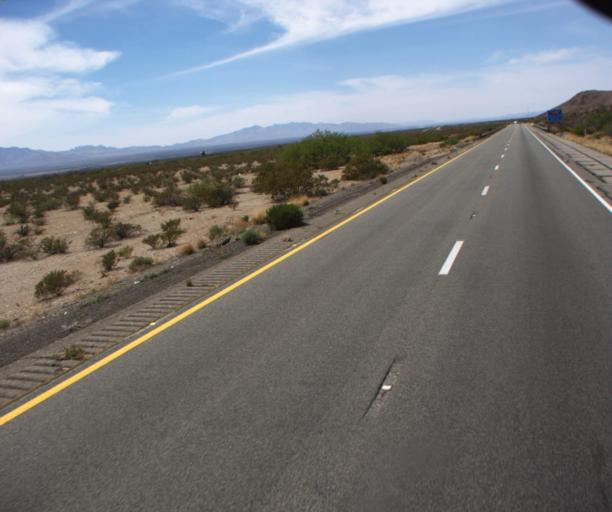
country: US
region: New Mexico
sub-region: Hidalgo County
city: Lordsburg
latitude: 32.2351
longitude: -109.0742
